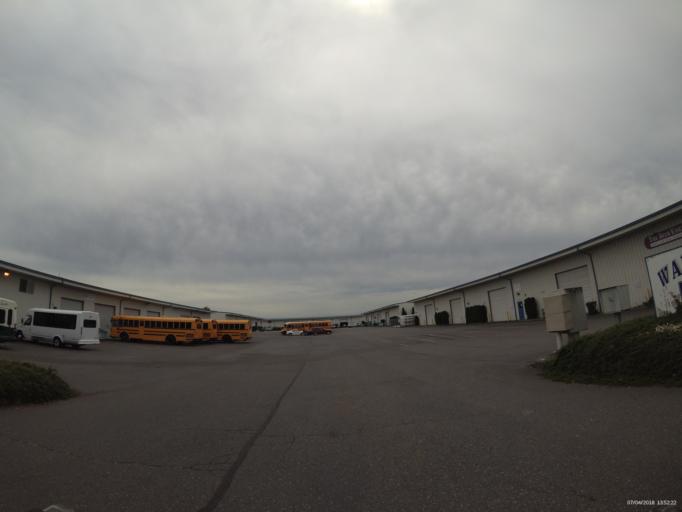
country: US
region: Washington
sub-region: Pierce County
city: McChord Air Force Base
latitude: 47.1558
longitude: -122.4725
